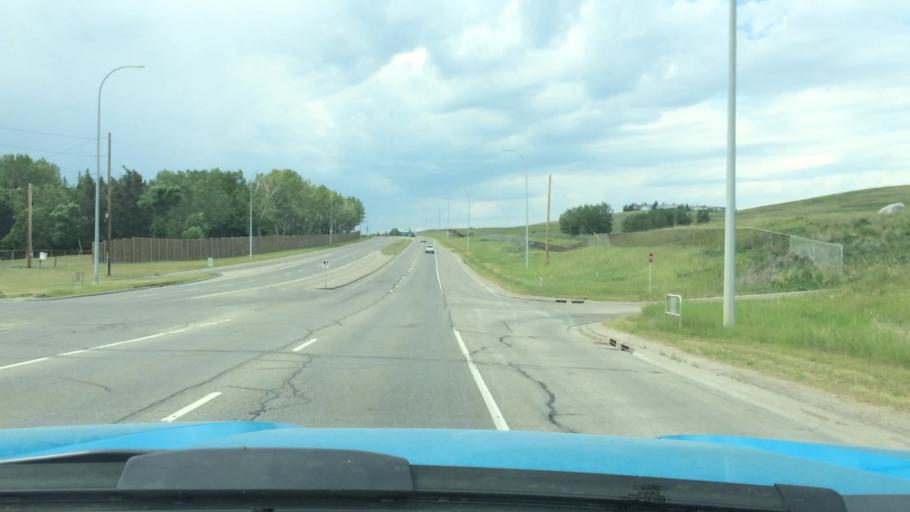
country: CA
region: Alberta
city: Calgary
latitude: 51.1030
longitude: -114.1268
